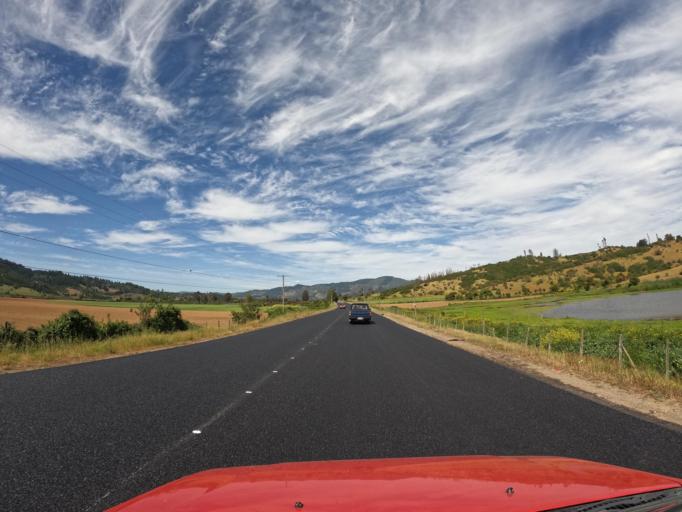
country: CL
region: Maule
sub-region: Provincia de Talca
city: Talca
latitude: -35.0993
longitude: -71.9982
